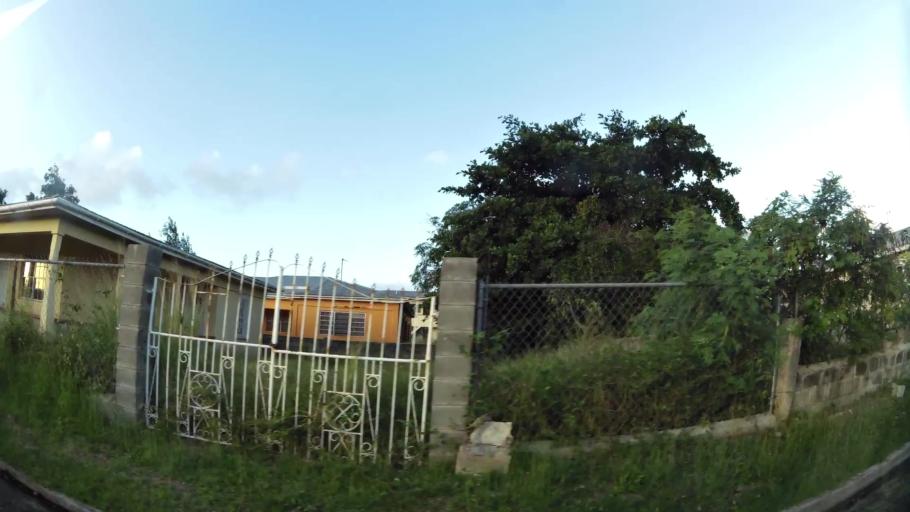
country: AG
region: Saint John
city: Saint John's
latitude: 17.1272
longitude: -61.8425
